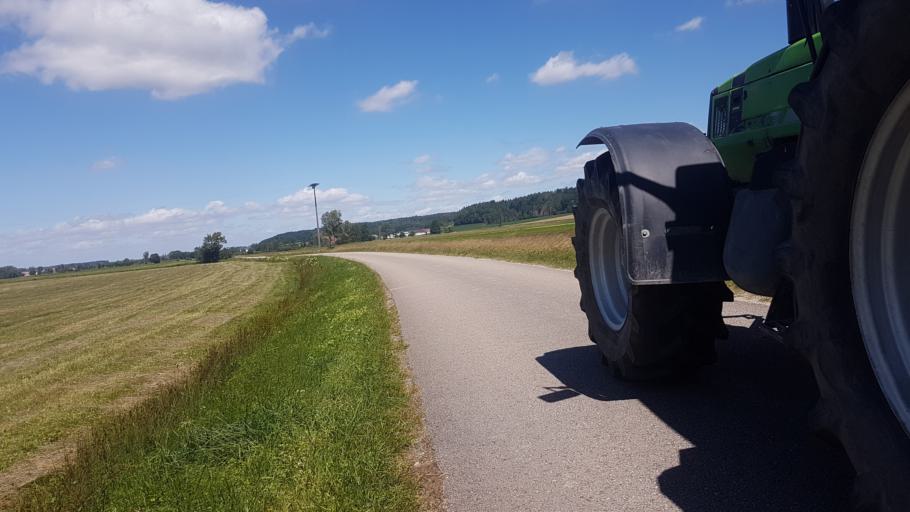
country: DE
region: Bavaria
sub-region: Regierungsbezirk Mittelfranken
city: Aurach
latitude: 49.2669
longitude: 10.4452
